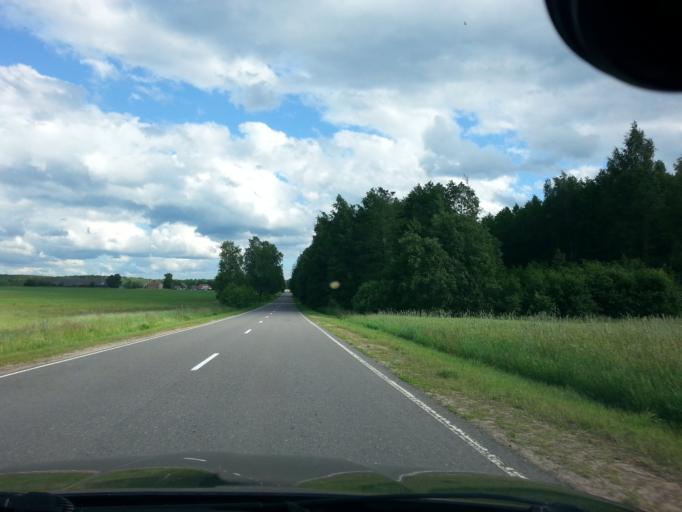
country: BY
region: Minsk
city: Svir
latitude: 54.9384
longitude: 26.3743
